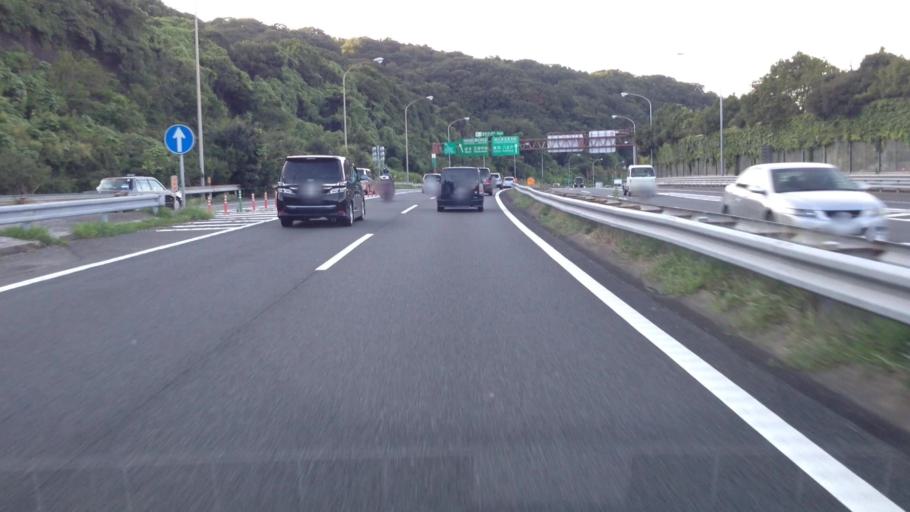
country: JP
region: Kanagawa
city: Zushi
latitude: 35.3372
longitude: 139.5909
